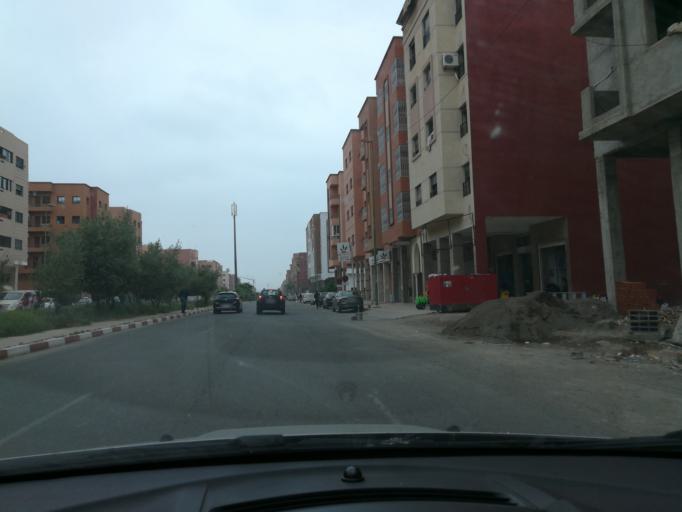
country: MA
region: Marrakech-Tensift-Al Haouz
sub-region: Marrakech
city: Marrakesh
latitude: 31.6709
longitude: -8.0280
